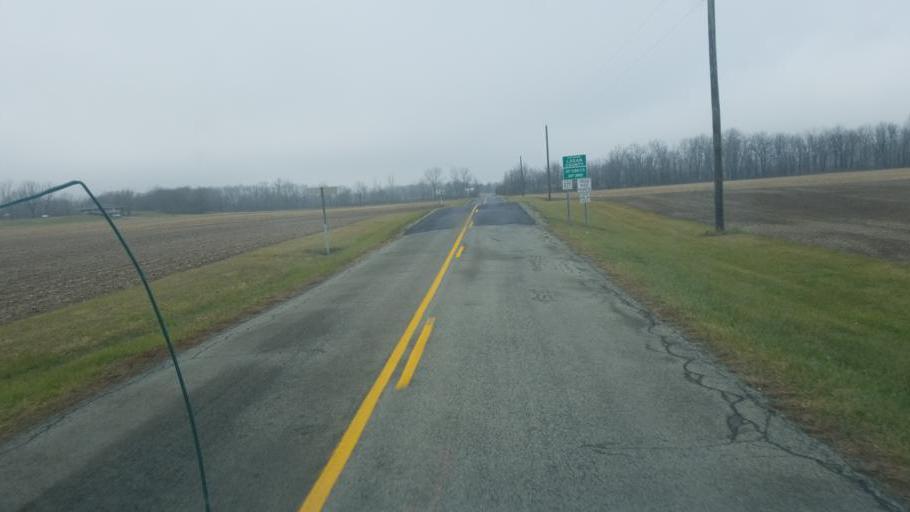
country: US
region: Ohio
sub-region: Champaign County
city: North Lewisburg
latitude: 40.2564
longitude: -83.5481
